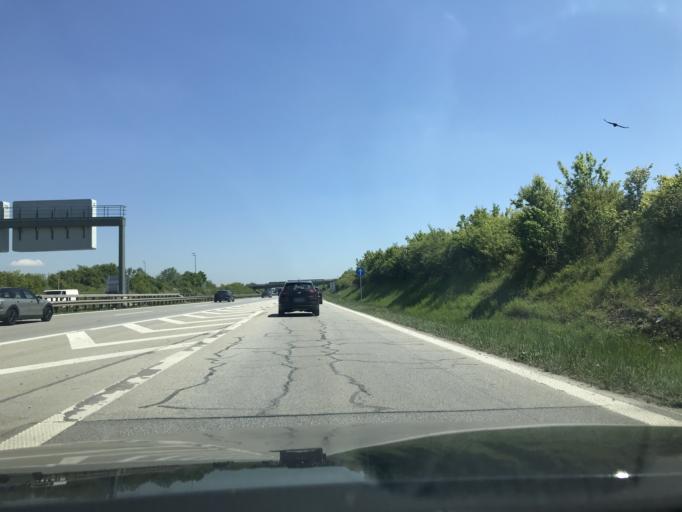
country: DE
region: Bavaria
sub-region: Upper Bavaria
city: Feldkirchen
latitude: 48.1419
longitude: 11.7138
